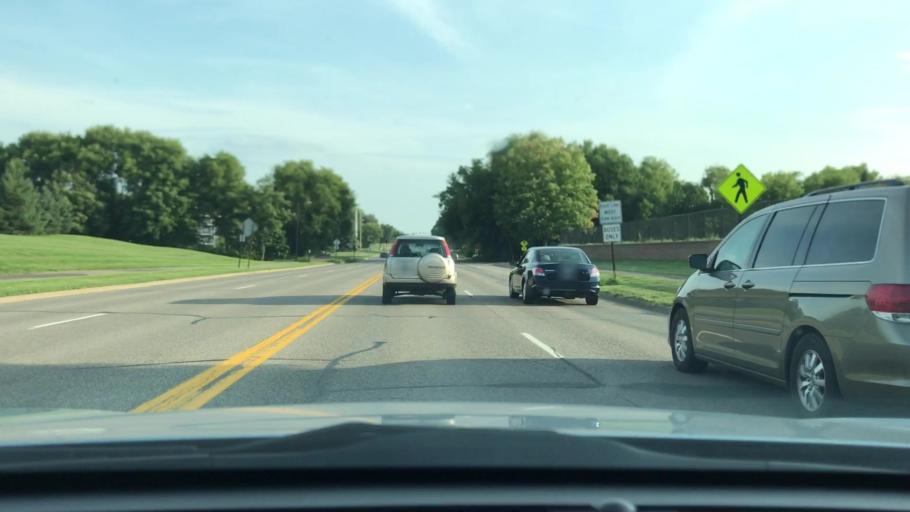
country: US
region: Minnesota
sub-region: Hennepin County
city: Plymouth
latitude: 45.0305
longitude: -93.4818
